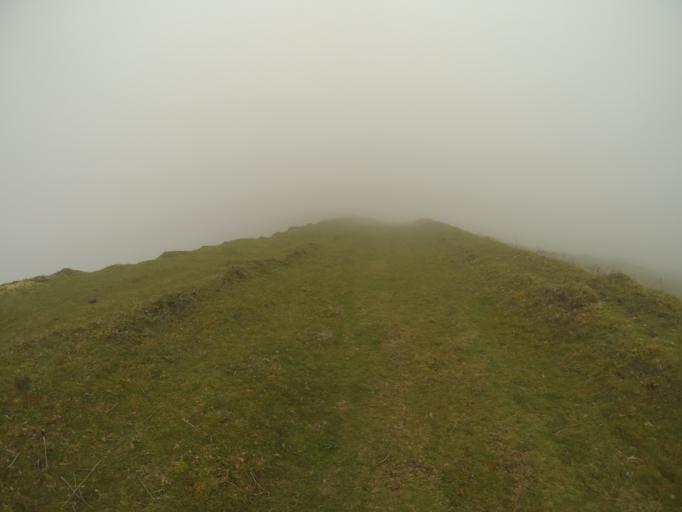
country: PT
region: Madeira
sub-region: Porto Moniz
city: Porto Moniz
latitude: 32.8132
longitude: -17.1442
